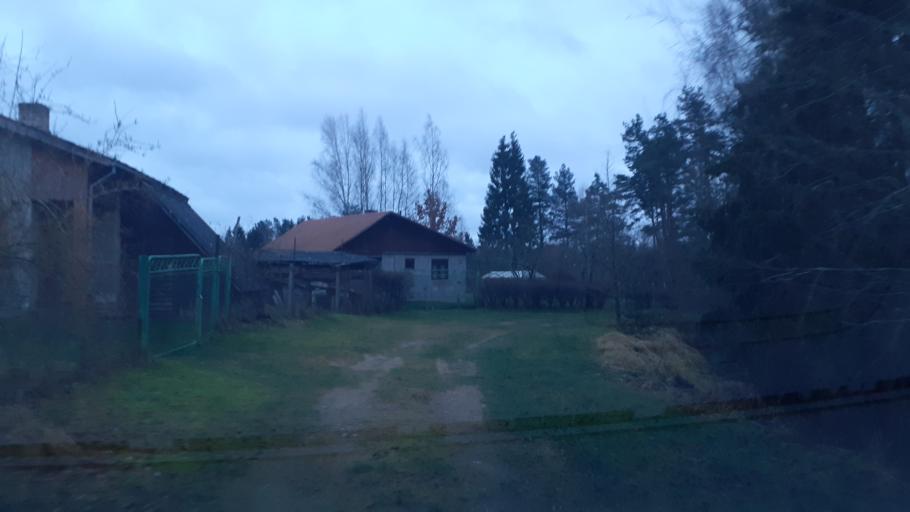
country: LV
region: Kuldigas Rajons
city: Kuldiga
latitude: 56.9943
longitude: 22.0362
